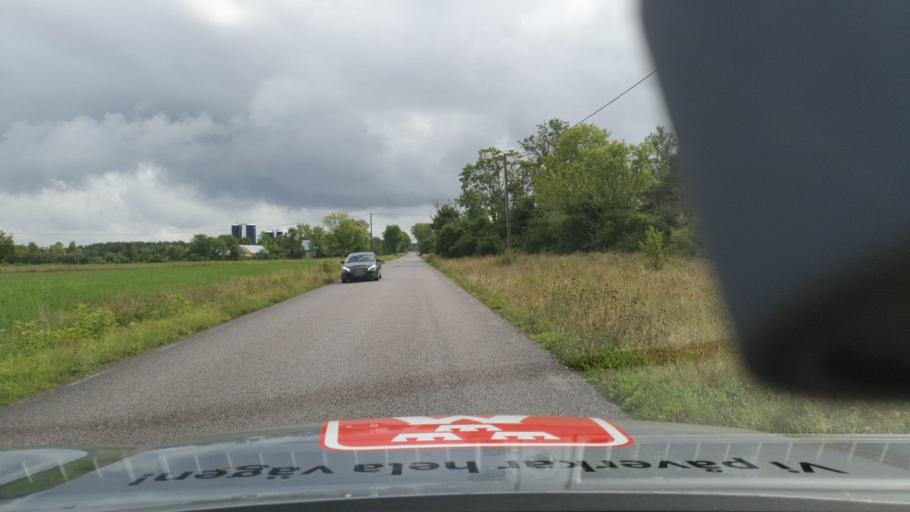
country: SE
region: Gotland
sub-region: Gotland
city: Slite
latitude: 57.6932
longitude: 18.7605
